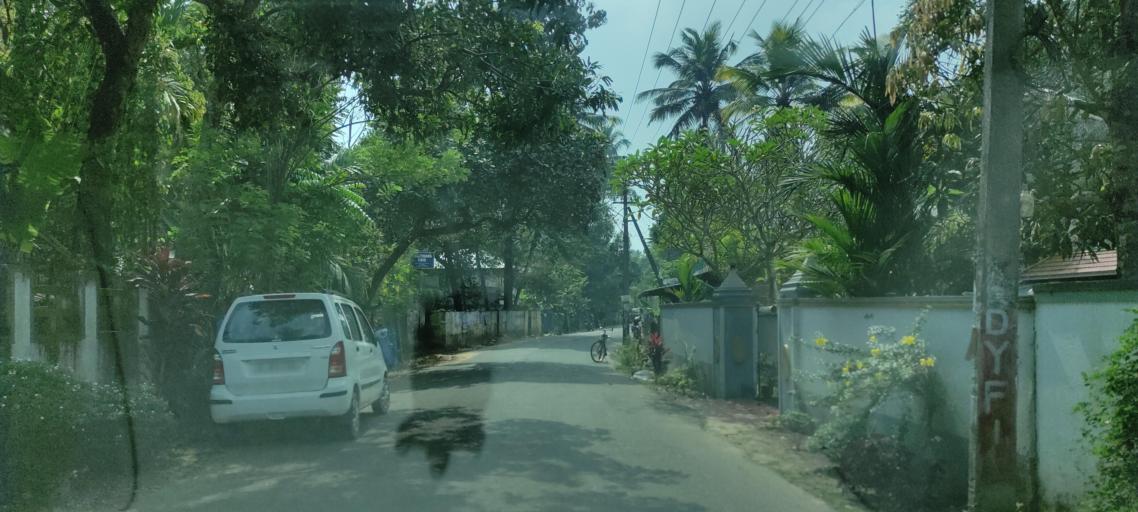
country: IN
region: Kerala
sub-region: Alappuzha
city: Shertallai
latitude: 9.6517
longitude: 76.3569
